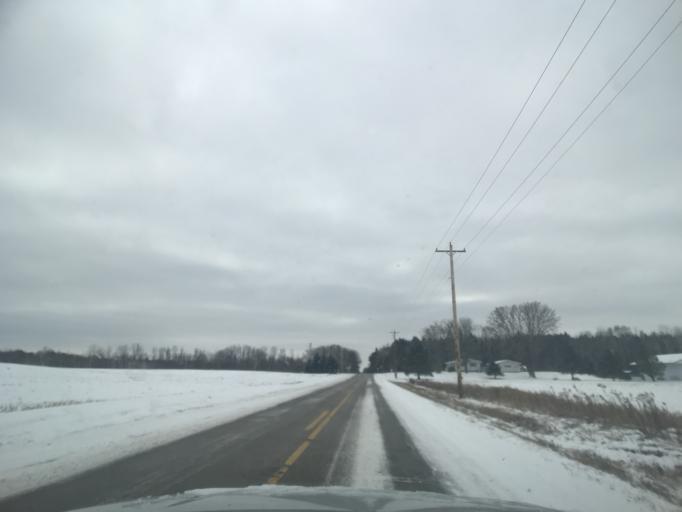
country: US
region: Wisconsin
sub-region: Brown County
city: Suamico
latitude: 44.7077
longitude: -88.0713
